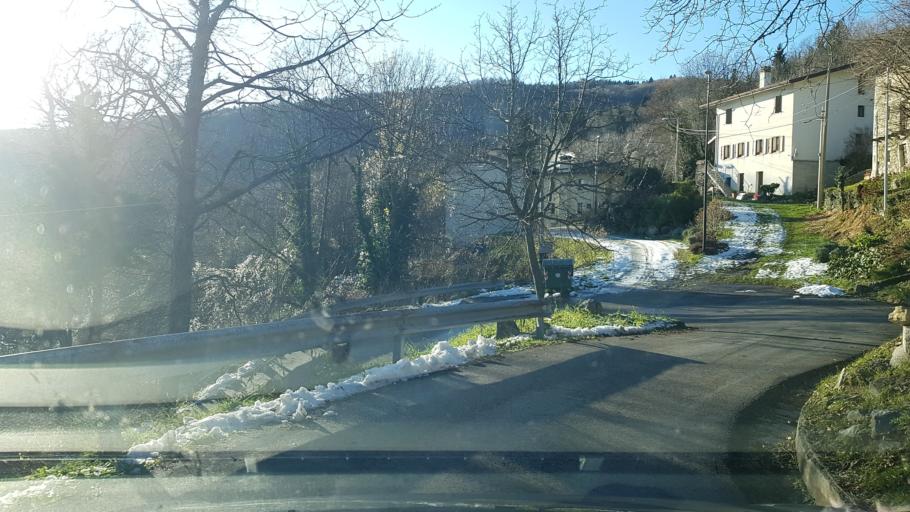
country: IT
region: Friuli Venezia Giulia
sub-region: Provincia di Udine
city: Savogna
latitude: 46.1863
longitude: 13.5336
